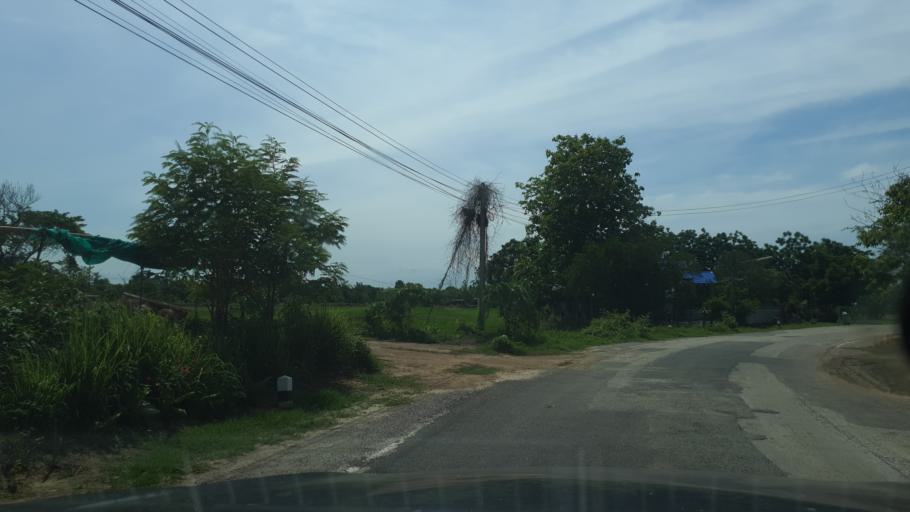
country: TH
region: Sukhothai
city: Si Samrong
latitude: 17.1964
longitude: 99.7298
